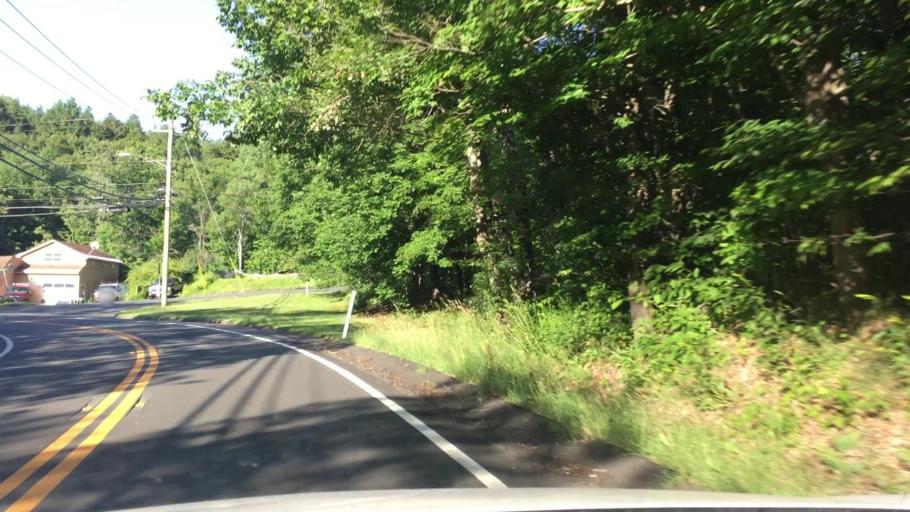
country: US
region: Massachusetts
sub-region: Berkshire County
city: Becket
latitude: 42.3154
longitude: -73.0937
